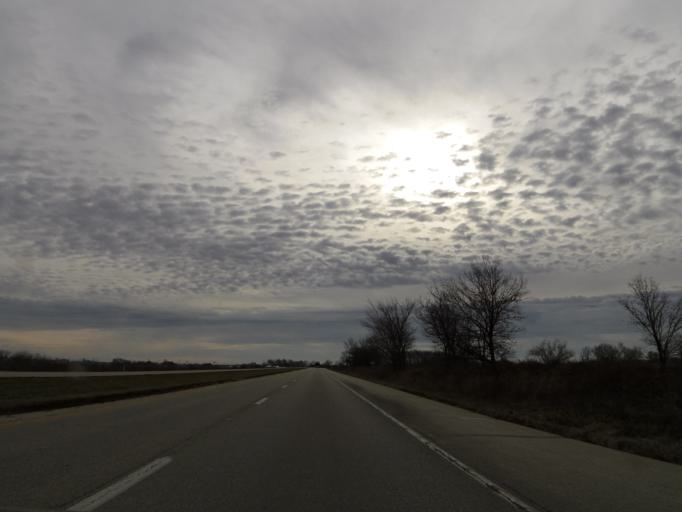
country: US
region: Indiana
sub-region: Boone County
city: Thorntown
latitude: 39.9501
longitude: -86.6342
